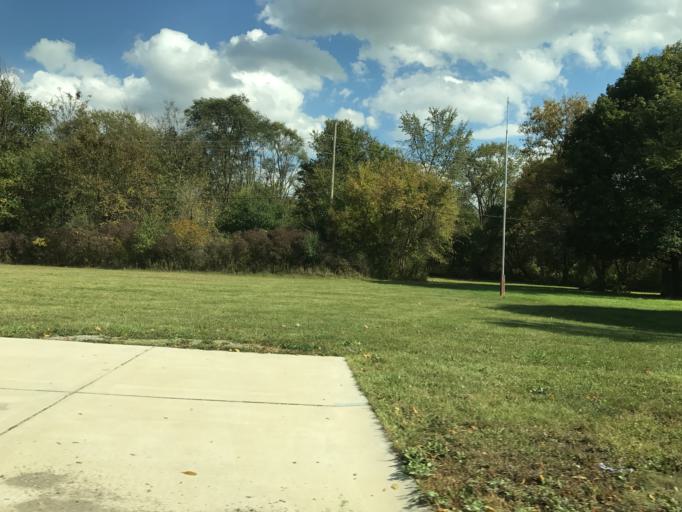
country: US
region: Michigan
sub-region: Oakland County
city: South Lyon
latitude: 42.5068
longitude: -83.6154
